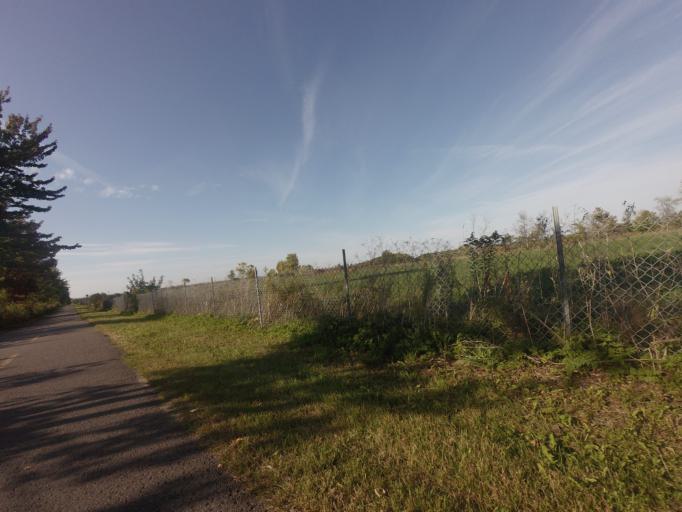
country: CA
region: Quebec
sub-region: Laurentides
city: Blainville
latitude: 45.7174
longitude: -73.9258
